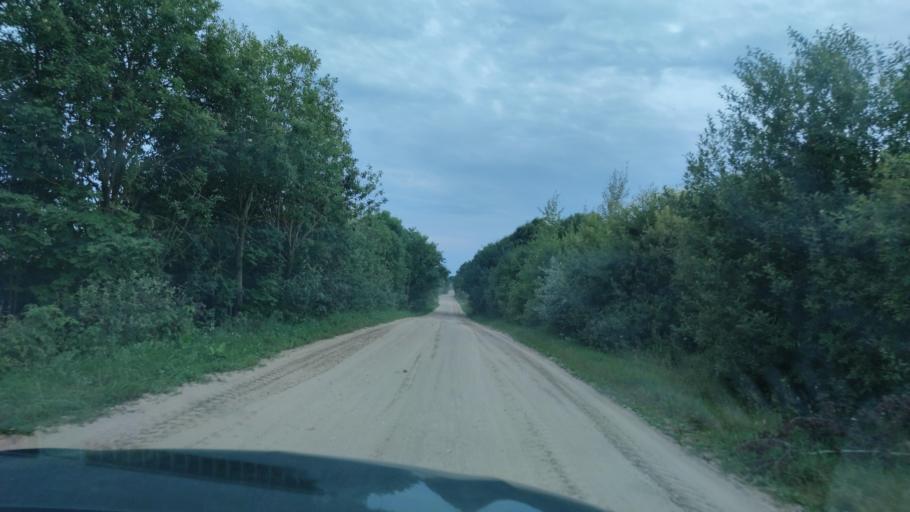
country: BY
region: Minsk
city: Myadzyel
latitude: 55.0938
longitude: 27.1329
